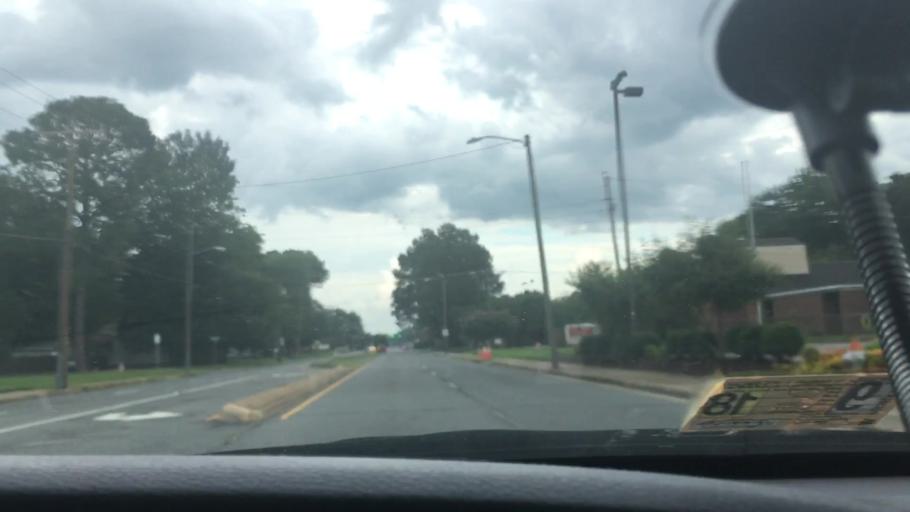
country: US
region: Virginia
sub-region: City of Portsmouth
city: Portsmouth Heights
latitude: 36.8191
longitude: -76.3777
